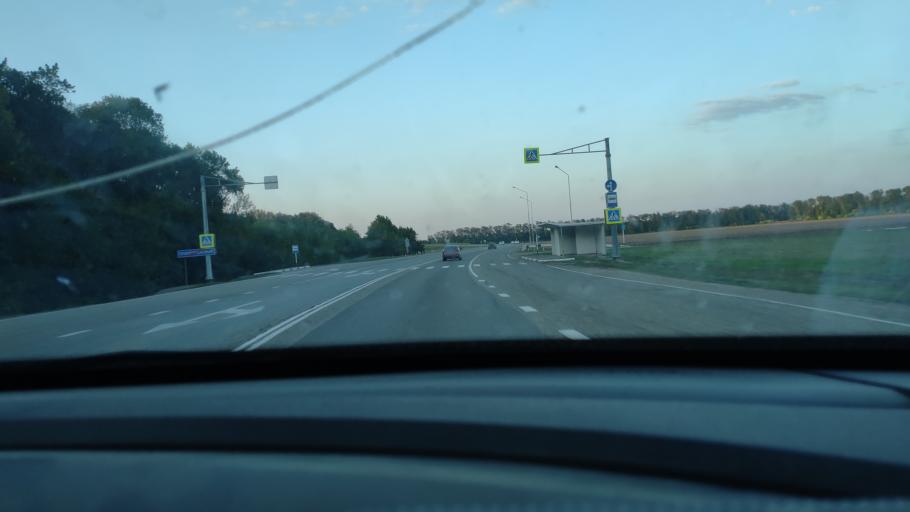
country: RU
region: Krasnodarskiy
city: Novominskaya
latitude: 46.4121
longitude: 39.0050
